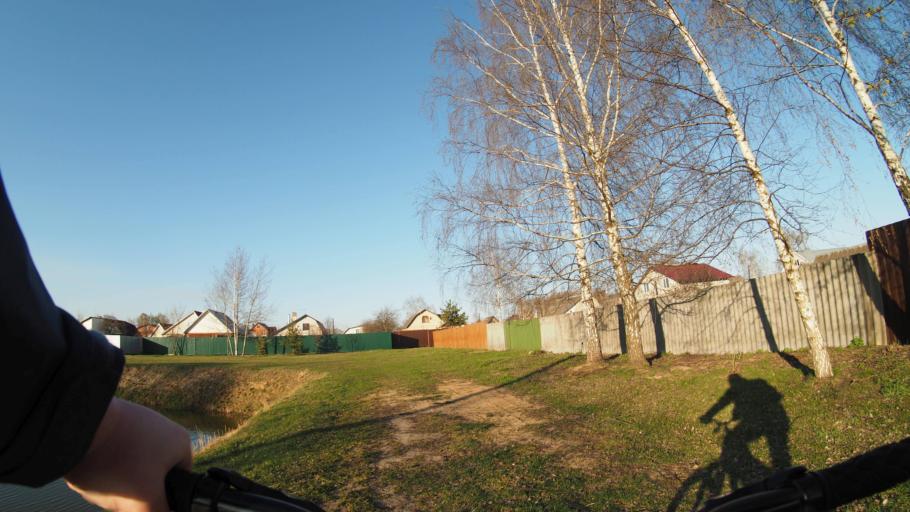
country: RU
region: Moskovskaya
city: Malyshevo
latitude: 55.4961
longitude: 38.3513
